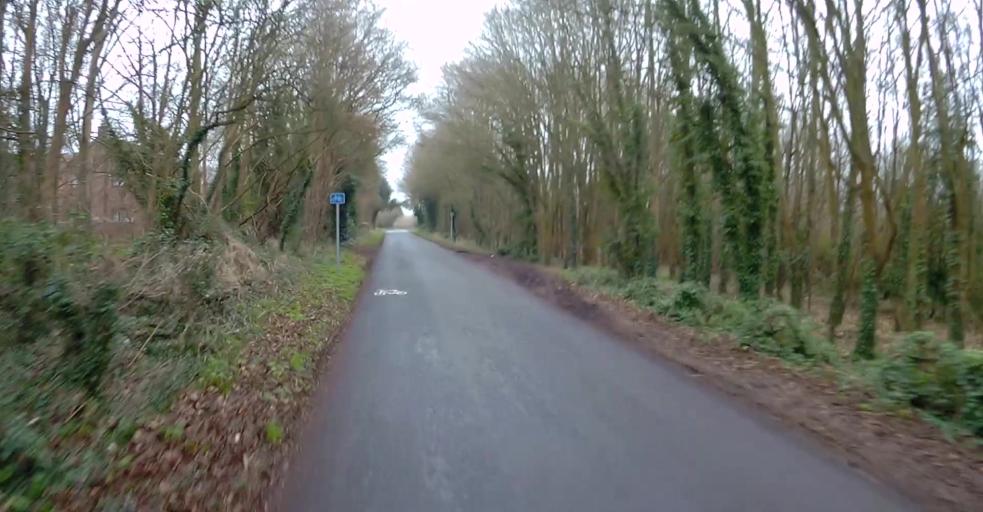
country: GB
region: England
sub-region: Hampshire
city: Old Basing
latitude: 51.2730
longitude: -1.0573
